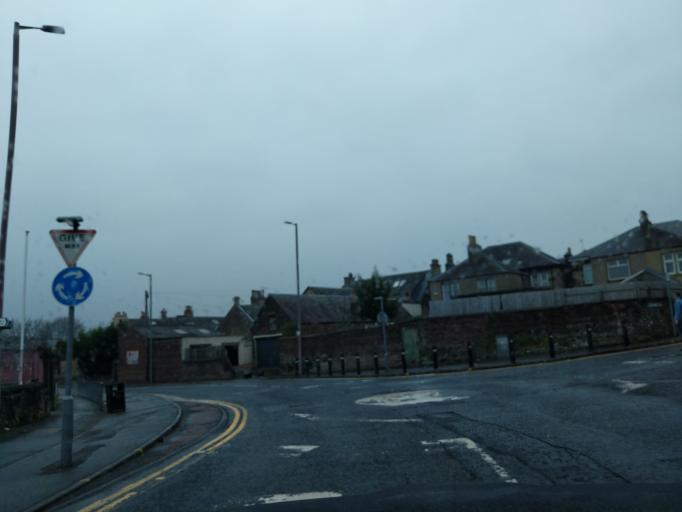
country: GB
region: Scotland
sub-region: Falkirk
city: Falkirk
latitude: 55.9952
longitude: -3.7849
